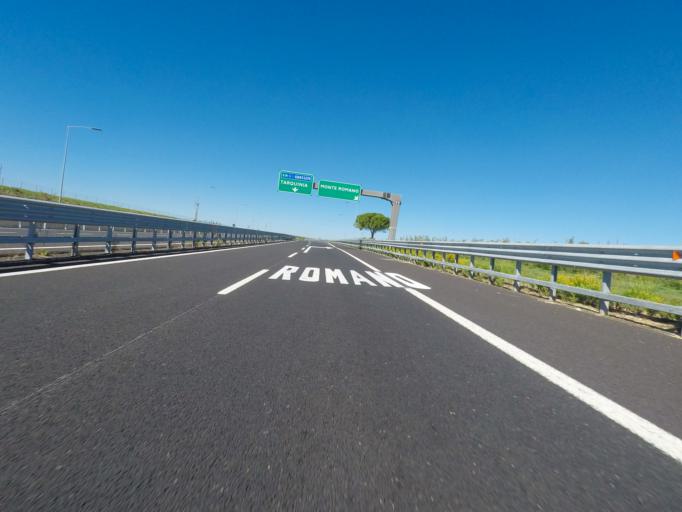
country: IT
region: Latium
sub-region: Provincia di Viterbo
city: Tarquinia
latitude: 42.2067
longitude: 11.7836
